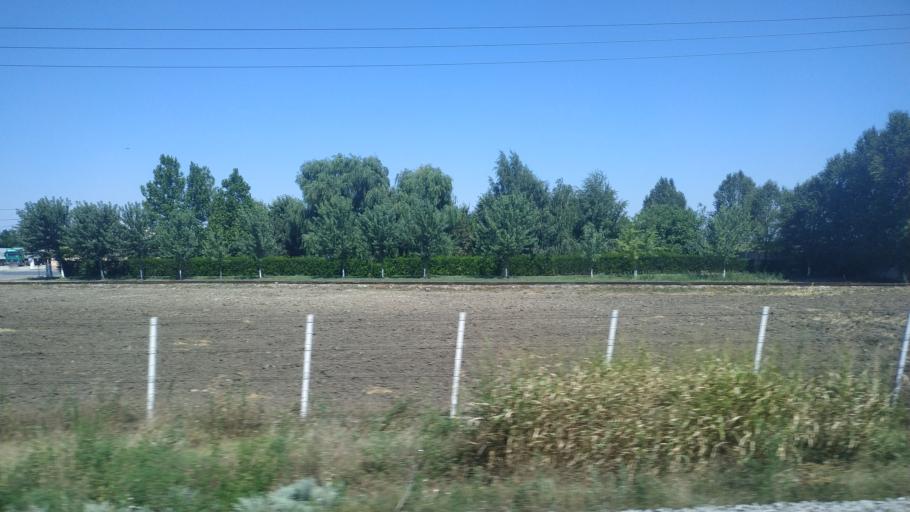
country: RO
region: Calarasi
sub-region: Comuna Borcea
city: Borcea
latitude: 44.4203
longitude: 27.6906
